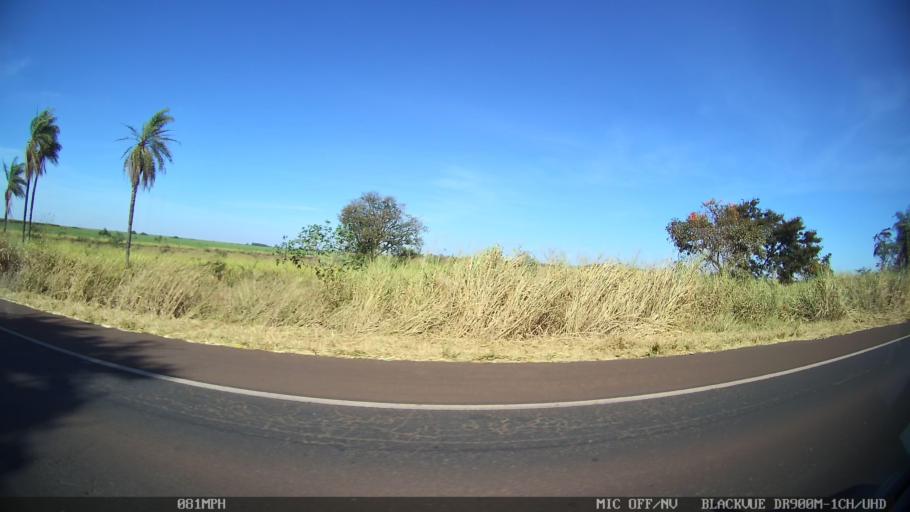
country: BR
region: Sao Paulo
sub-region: Barretos
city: Barretos
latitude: -20.4680
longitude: -48.4801
